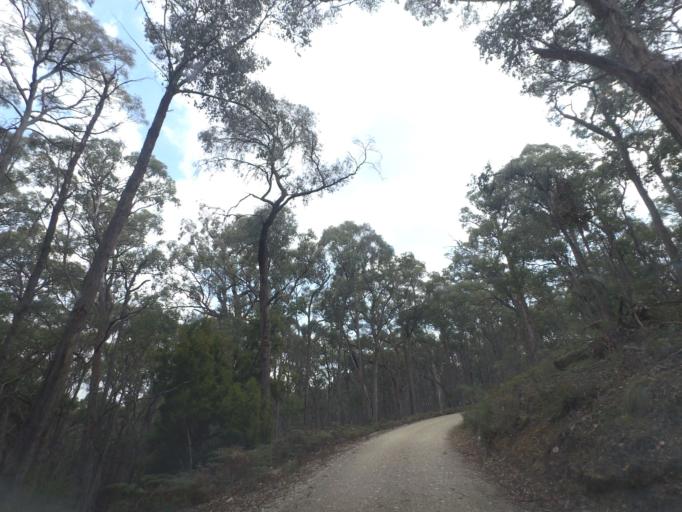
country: AU
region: Victoria
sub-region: Moorabool
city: Bacchus Marsh
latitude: -37.4609
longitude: 144.3598
